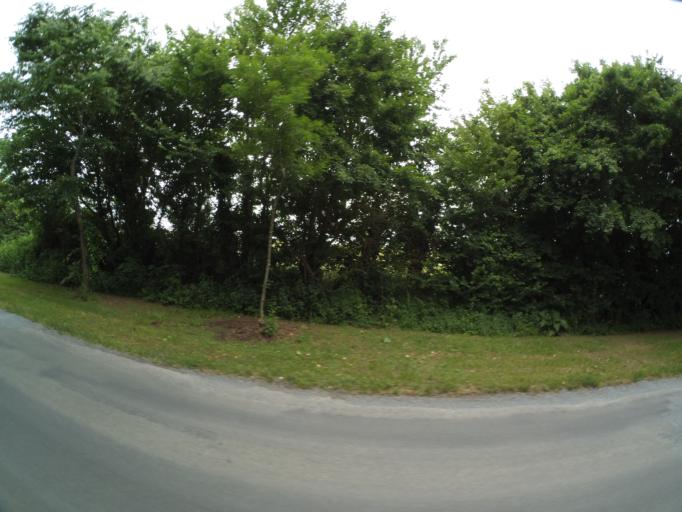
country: FR
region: Poitou-Charentes
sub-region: Departement de la Charente-Maritime
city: Saint-Laurent-de-la-Pree
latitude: 45.9863
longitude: -1.0109
